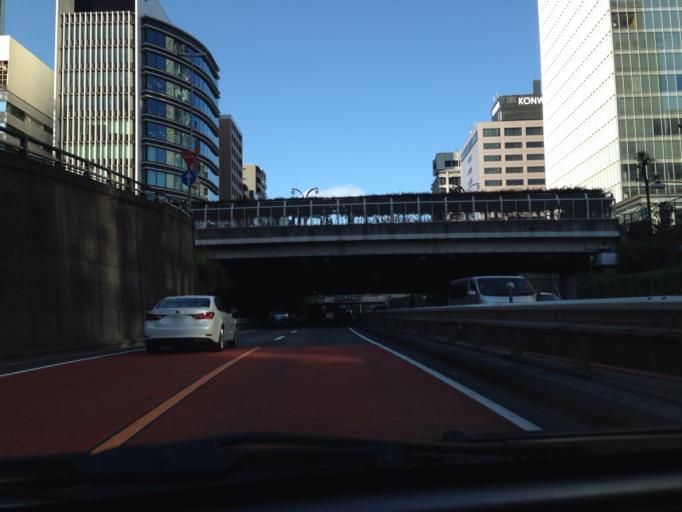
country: JP
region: Tokyo
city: Tokyo
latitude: 35.6678
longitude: 139.7679
